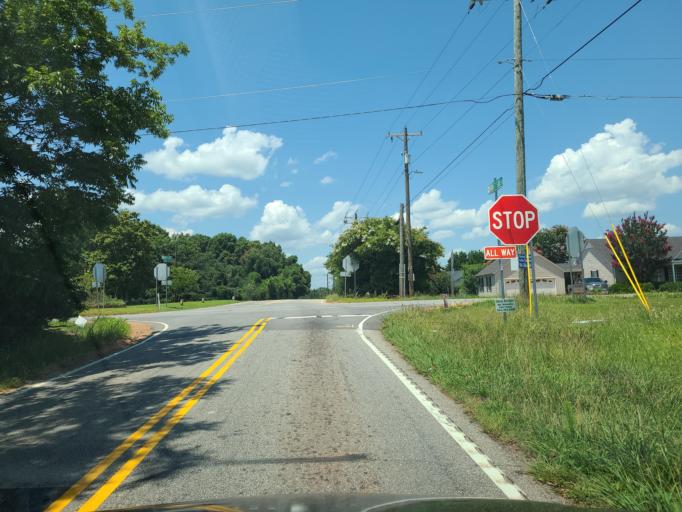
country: US
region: South Carolina
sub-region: Spartanburg County
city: Duncan
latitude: 34.9839
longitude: -82.1787
